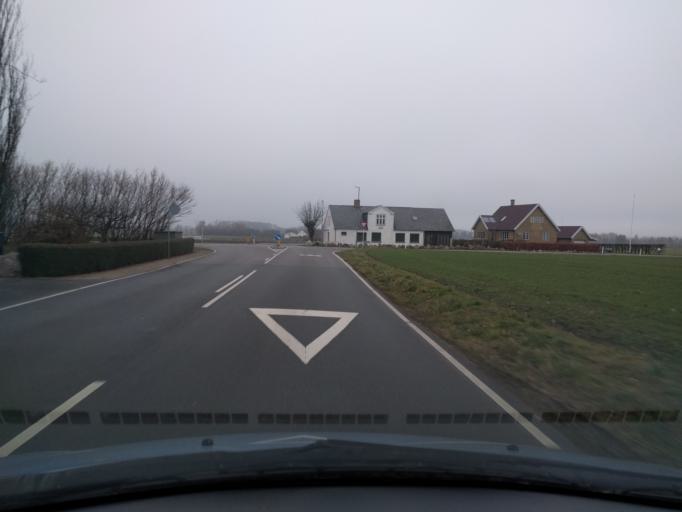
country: DK
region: South Denmark
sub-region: Odense Kommune
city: Bullerup
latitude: 55.3986
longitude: 10.5118
